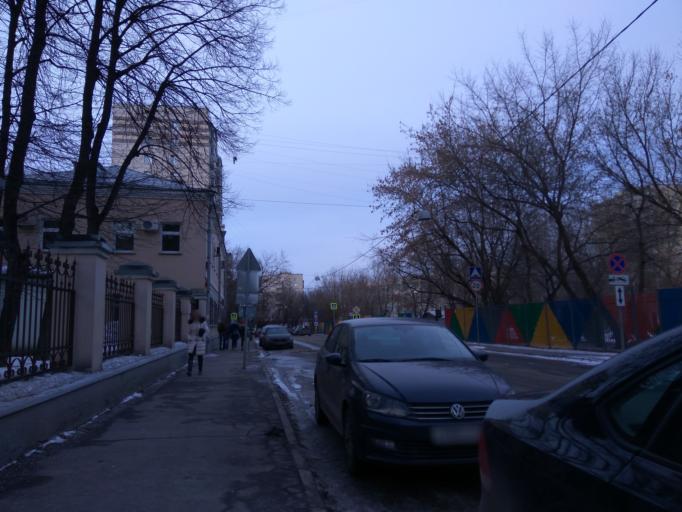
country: RU
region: Moscow
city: Mar'ina Roshcha
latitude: 55.7802
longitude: 37.6415
